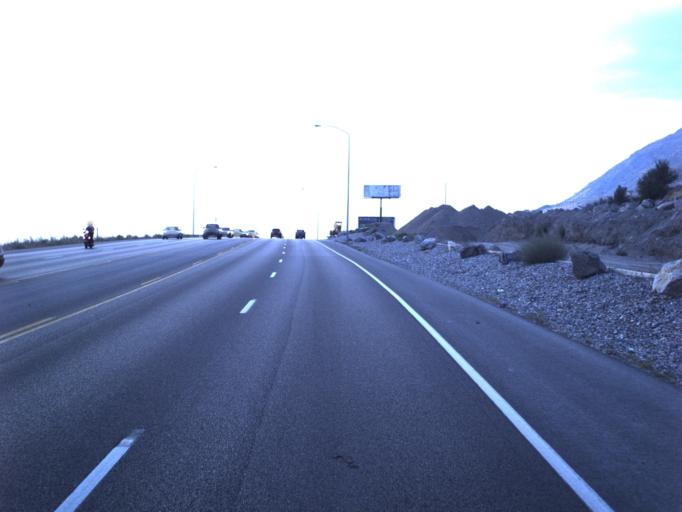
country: US
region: Utah
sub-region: Utah County
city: Springville
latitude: 40.1931
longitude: -111.6132
